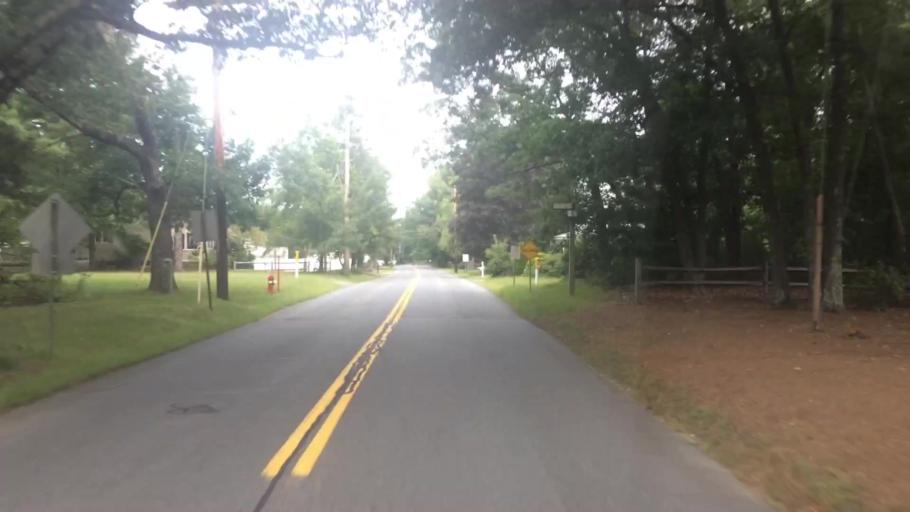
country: US
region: Massachusetts
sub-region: Middlesex County
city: West Concord
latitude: 42.4595
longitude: -71.4137
